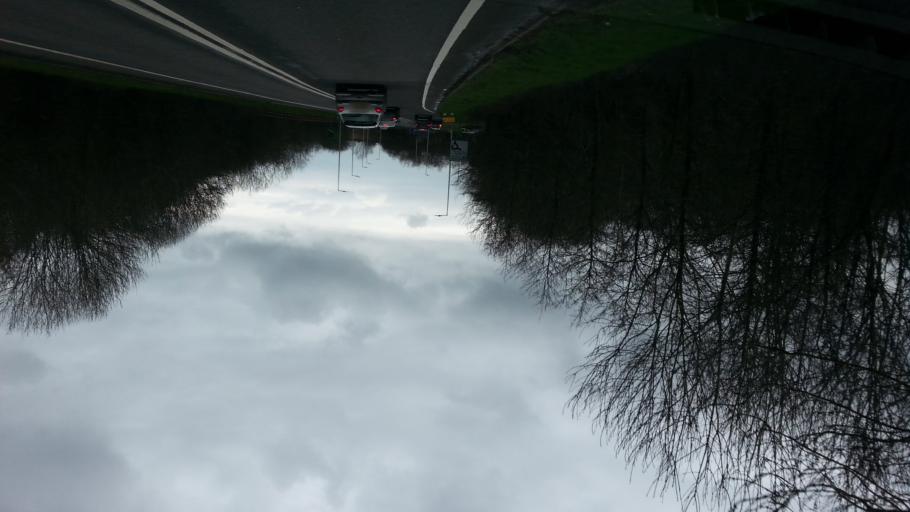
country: GB
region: England
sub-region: Devon
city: Barnstaple
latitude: 51.0717
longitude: -4.0291
